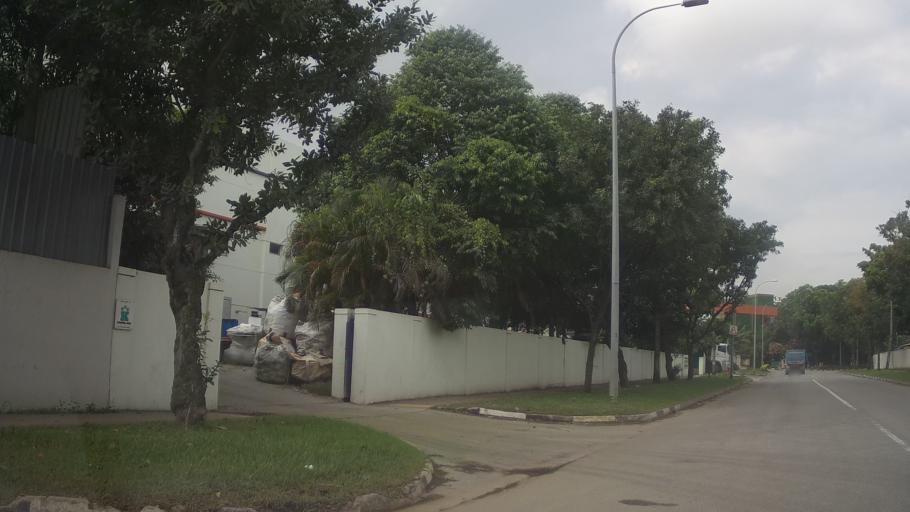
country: MY
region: Johor
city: Johor Bahru
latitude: 1.4342
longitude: 103.7506
